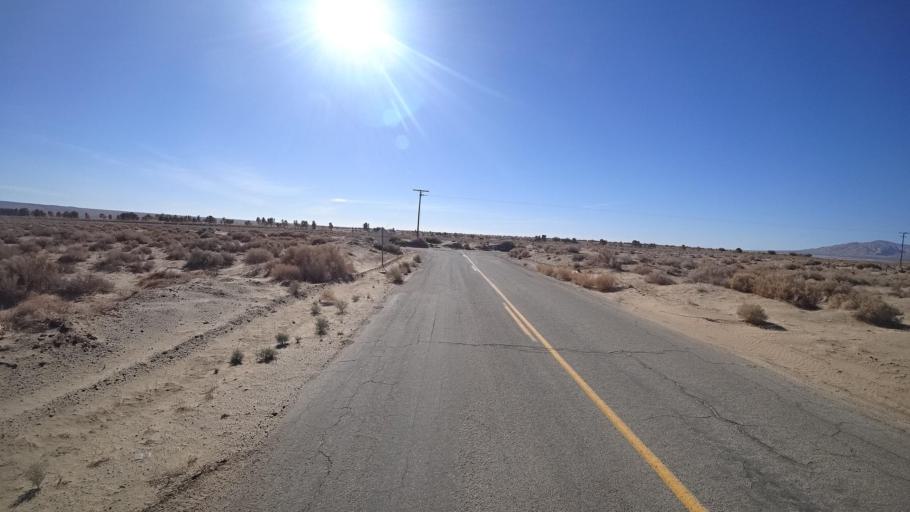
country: US
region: California
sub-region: Kern County
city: California City
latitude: 35.2874
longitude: -117.9680
